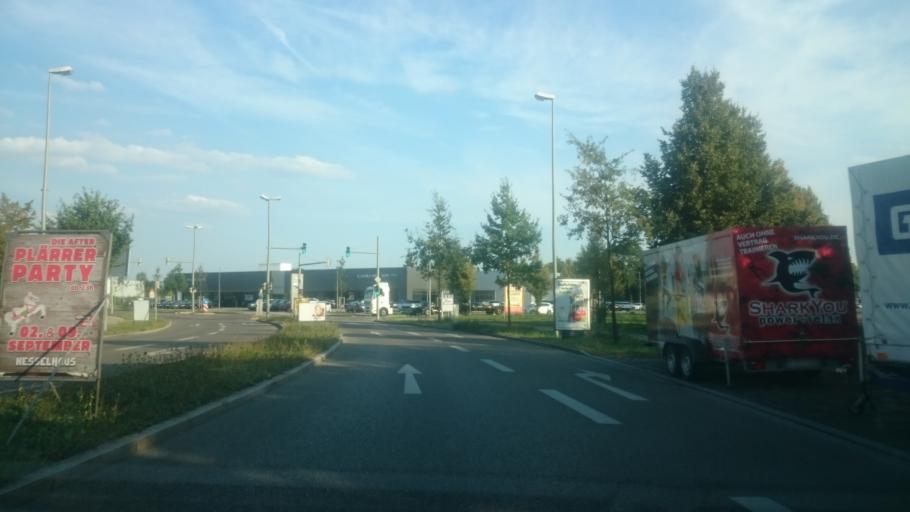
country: DE
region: Bavaria
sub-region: Swabia
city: Augsburg
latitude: 48.3820
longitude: 10.9360
